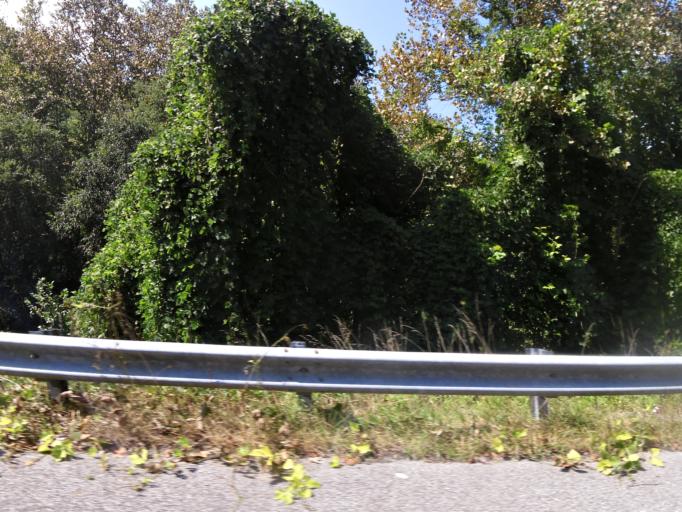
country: US
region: Kentucky
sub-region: Harlan County
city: Harlan
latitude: 36.8545
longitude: -83.3166
